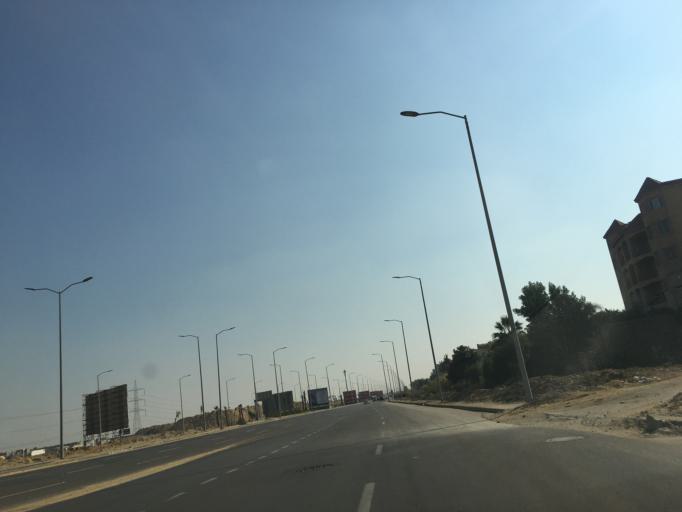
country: EG
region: Al Jizah
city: Awsim
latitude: 30.0040
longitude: 30.9855
